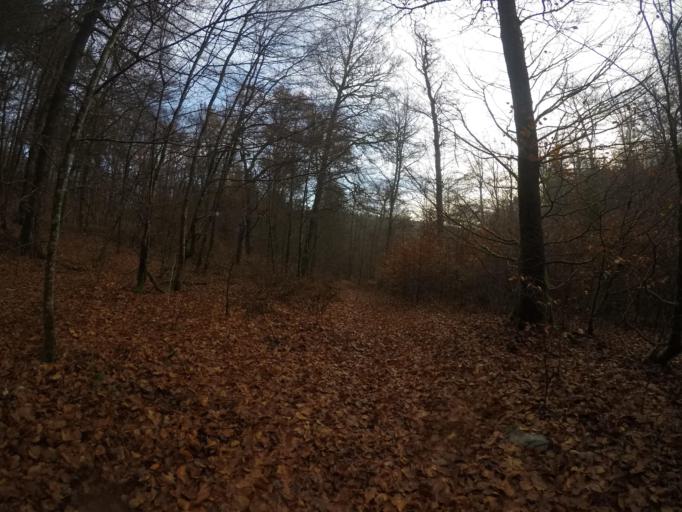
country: BE
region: Wallonia
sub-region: Province du Luxembourg
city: Habay-la-Vieille
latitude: 49.7544
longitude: 5.6084
